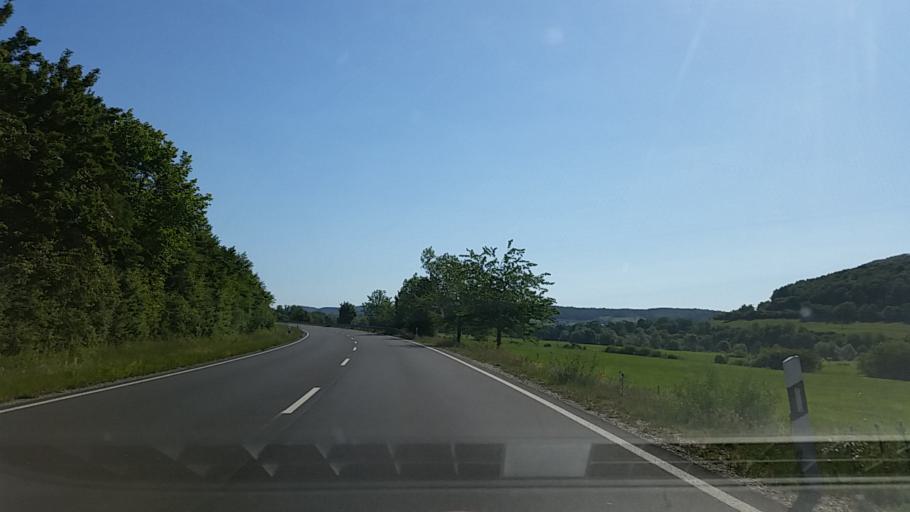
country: DE
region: Bavaria
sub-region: Regierungsbezirk Unterfranken
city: Hammelburg
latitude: 50.1080
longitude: 9.9026
